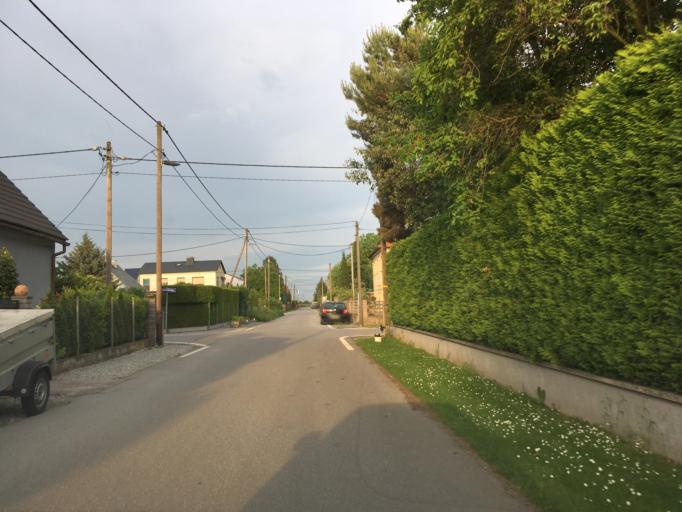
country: AT
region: Lower Austria
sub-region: Politischer Bezirk Wien-Umgebung
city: Gerasdorf bei Wien
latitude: 48.3132
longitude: 16.4982
